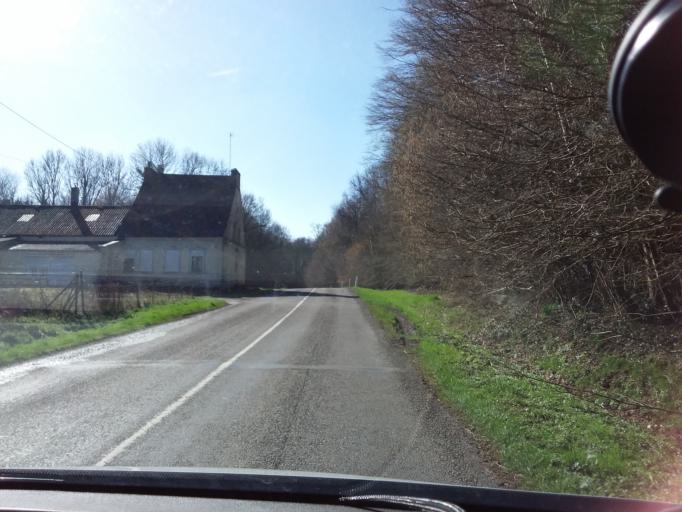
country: FR
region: Picardie
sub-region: Departement de l'Aisne
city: Hirson
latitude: 49.9521
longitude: 4.0781
